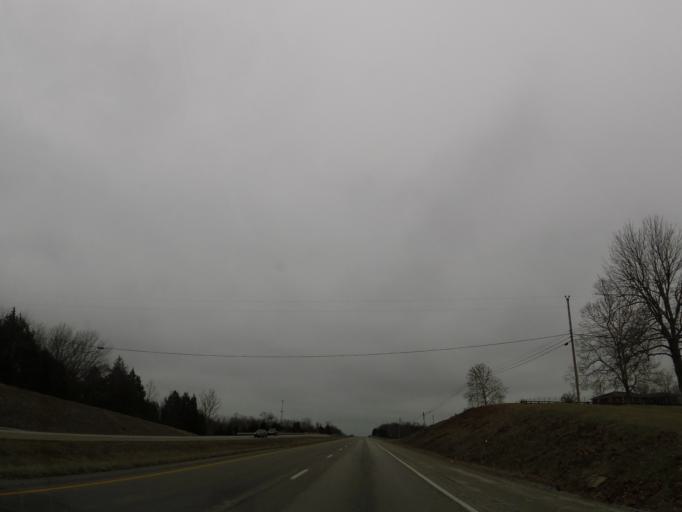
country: US
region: Kentucky
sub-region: Anderson County
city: Lawrenceburg
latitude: 37.9927
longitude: -84.8921
